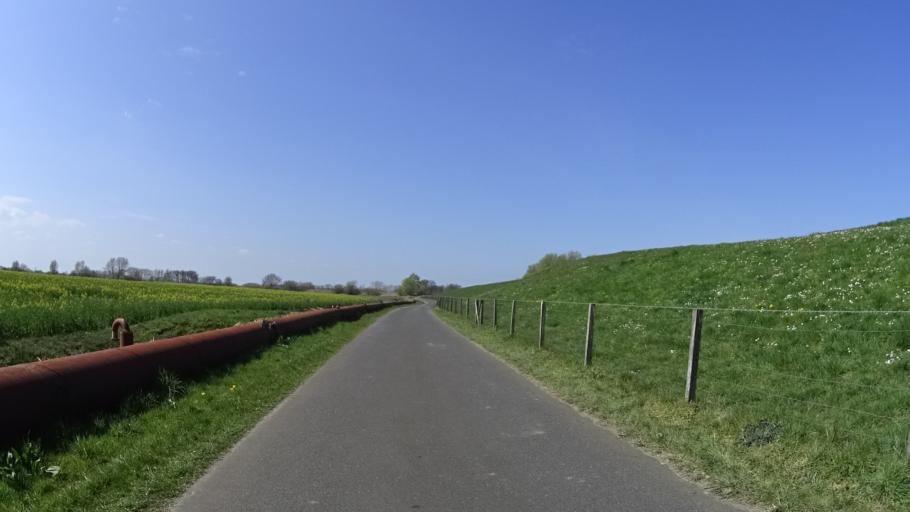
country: DE
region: Lower Saxony
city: Weener
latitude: 53.1001
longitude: 7.3359
